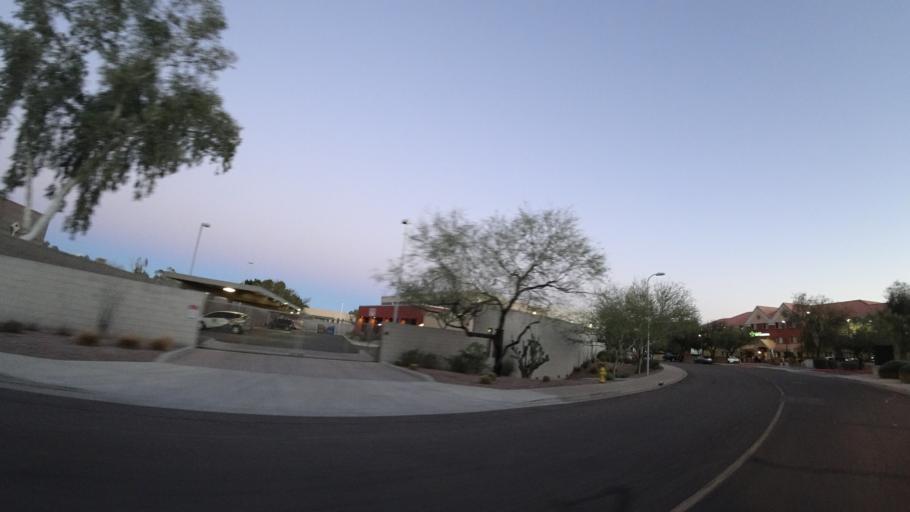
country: US
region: Arizona
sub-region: Maricopa County
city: Tempe Junction
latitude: 33.4128
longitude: -111.9729
